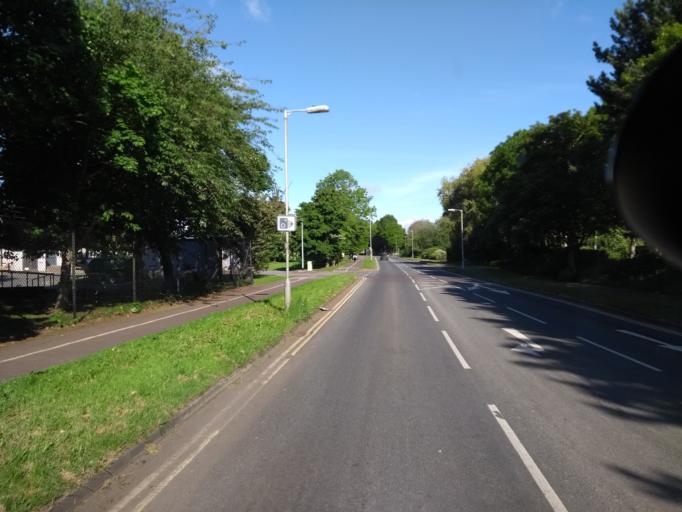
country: GB
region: England
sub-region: Somerset
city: Taunton
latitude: 51.0146
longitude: -3.0811
